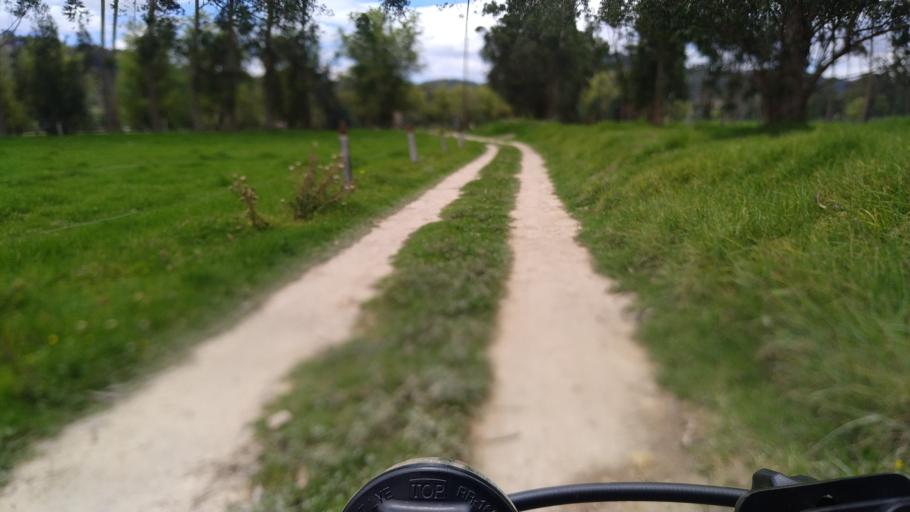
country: CO
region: Boyaca
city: Paipa
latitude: 5.7739
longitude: -73.0877
